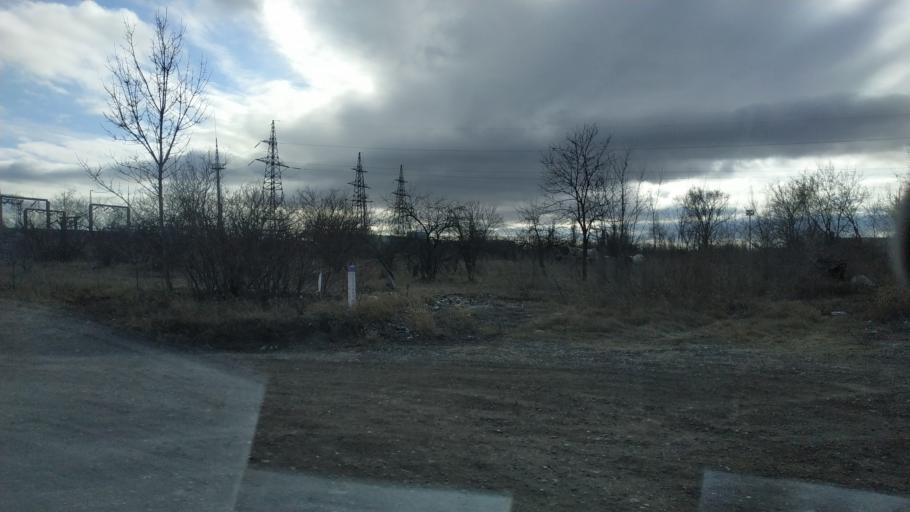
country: MD
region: Causeni
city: Causeni
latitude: 46.6622
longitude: 29.4213
